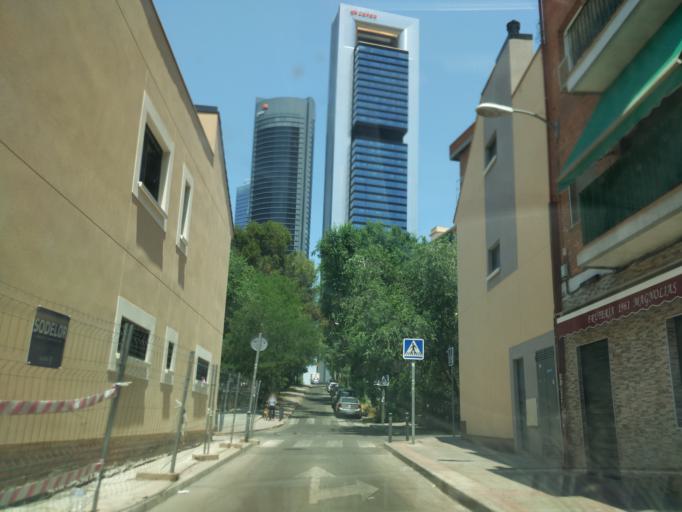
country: ES
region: Madrid
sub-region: Provincia de Madrid
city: Chamartin
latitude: 40.4729
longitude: -3.6898
